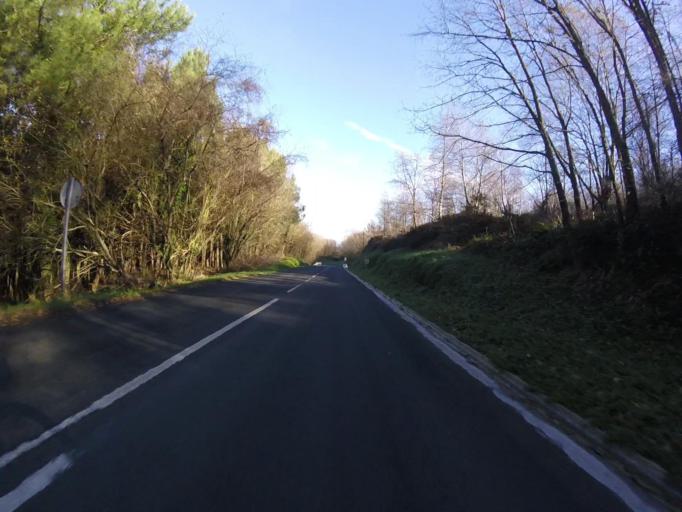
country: ES
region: Basque Country
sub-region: Provincia de Guipuzcoa
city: Fuenterrabia
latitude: 43.3637
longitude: -1.8322
